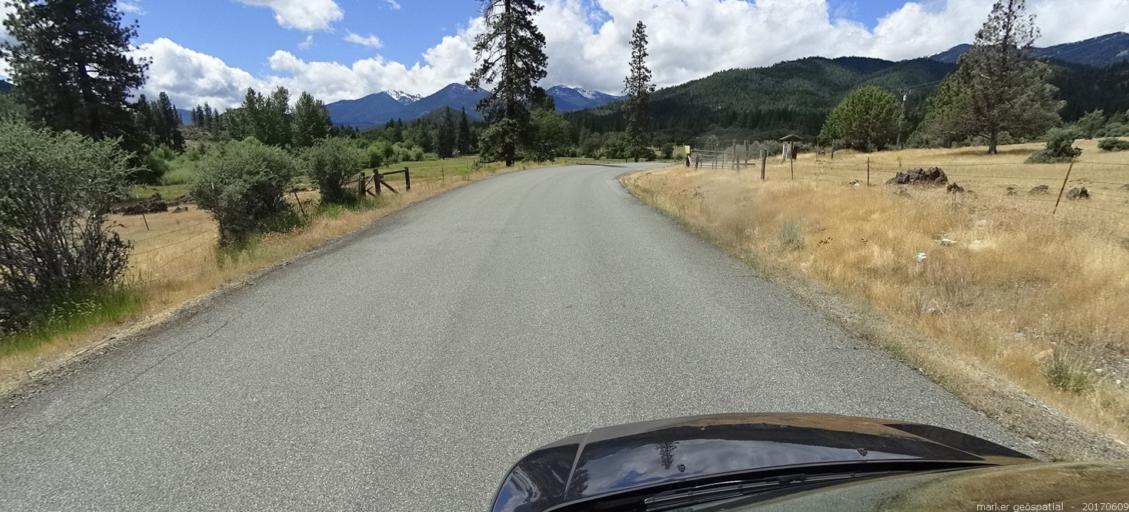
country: US
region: California
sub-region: Siskiyou County
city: Yreka
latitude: 41.4102
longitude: -122.8647
